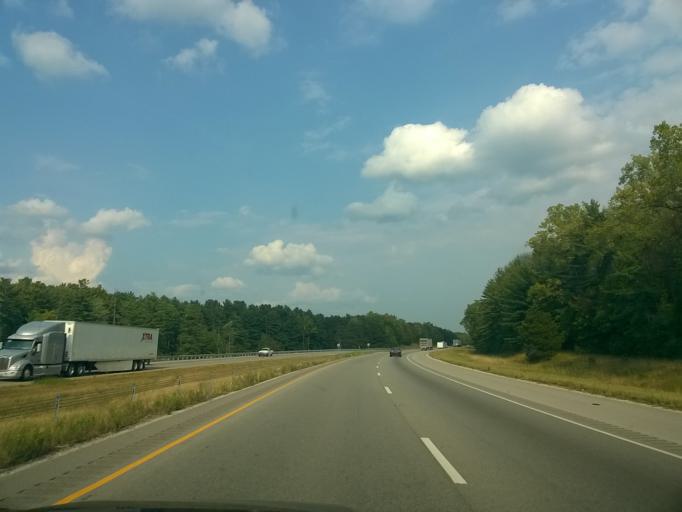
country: US
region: Indiana
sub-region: Vigo County
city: Seelyville
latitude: 39.4510
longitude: -87.1957
